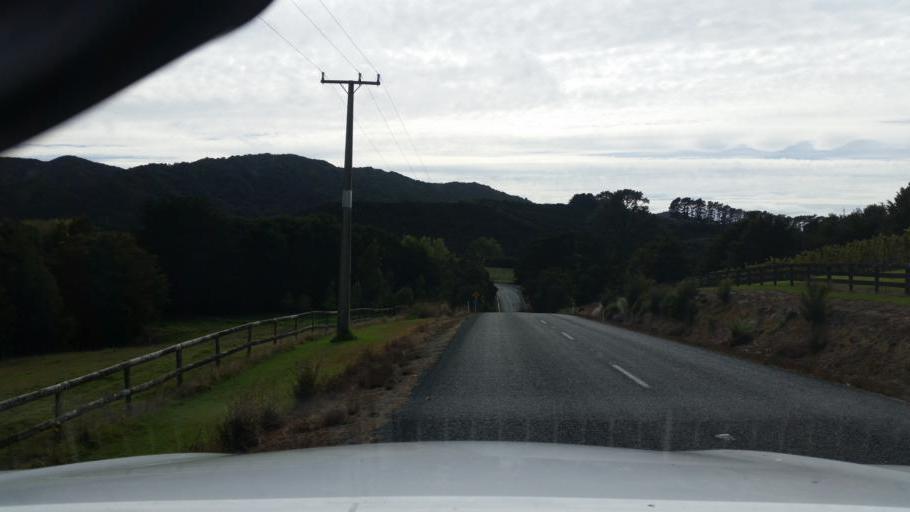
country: NZ
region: Auckland
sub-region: Auckland
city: Wellsford
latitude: -36.0885
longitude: 174.5344
